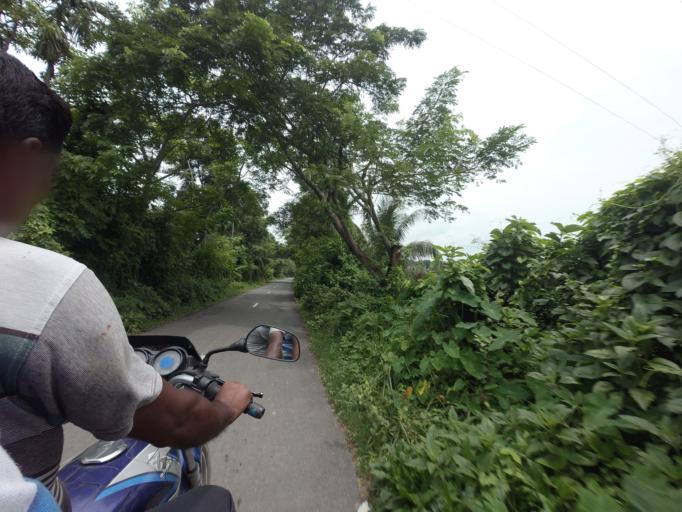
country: BD
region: Khulna
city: Kalia
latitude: 23.0896
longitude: 89.6583
